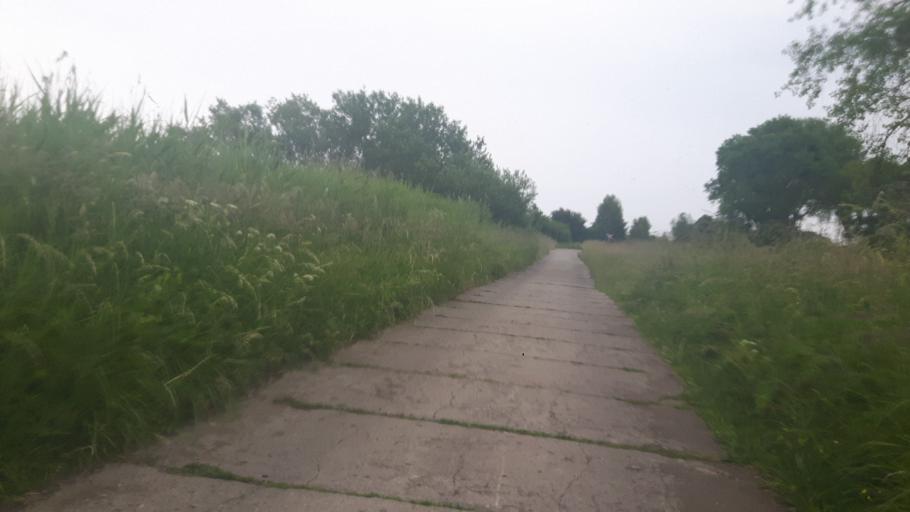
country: PL
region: Warmian-Masurian Voivodeship
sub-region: Powiat elblaski
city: Tolkmicko
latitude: 54.2920
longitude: 19.4569
